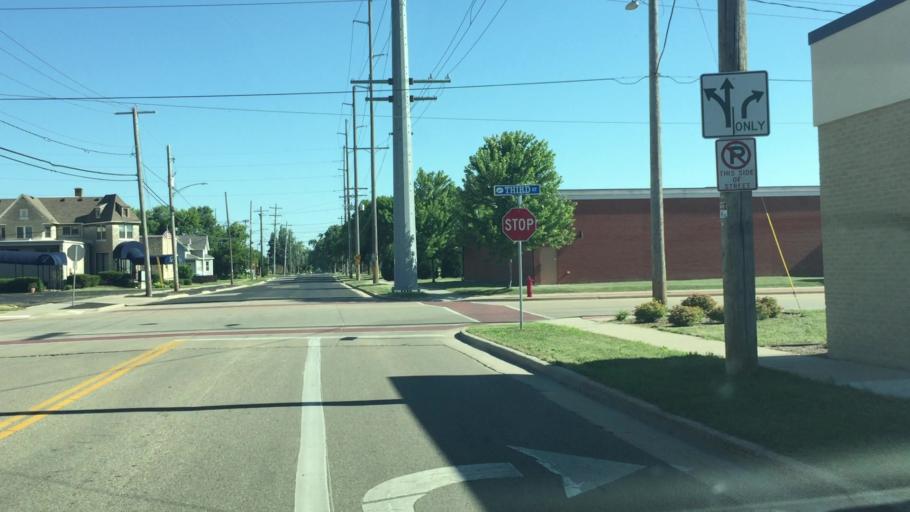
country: US
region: Wisconsin
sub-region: Winnebago County
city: Menasha
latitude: 44.2045
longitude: -88.4491
